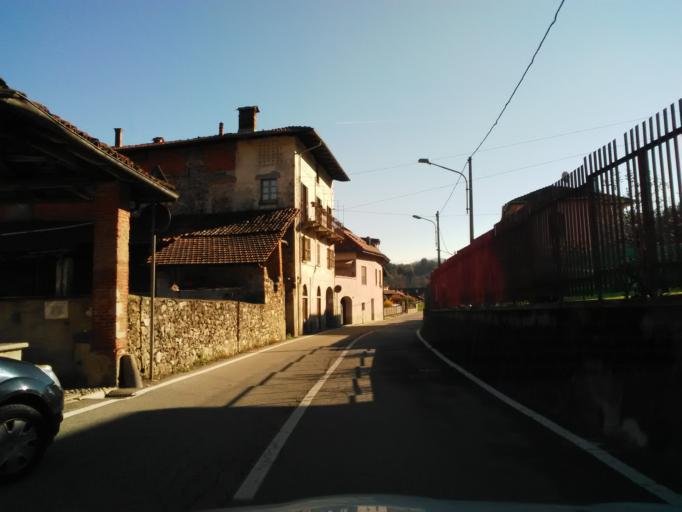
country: IT
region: Piedmont
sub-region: Provincia di Vercelli
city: Borgosesia
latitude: 45.7350
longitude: 8.2751
